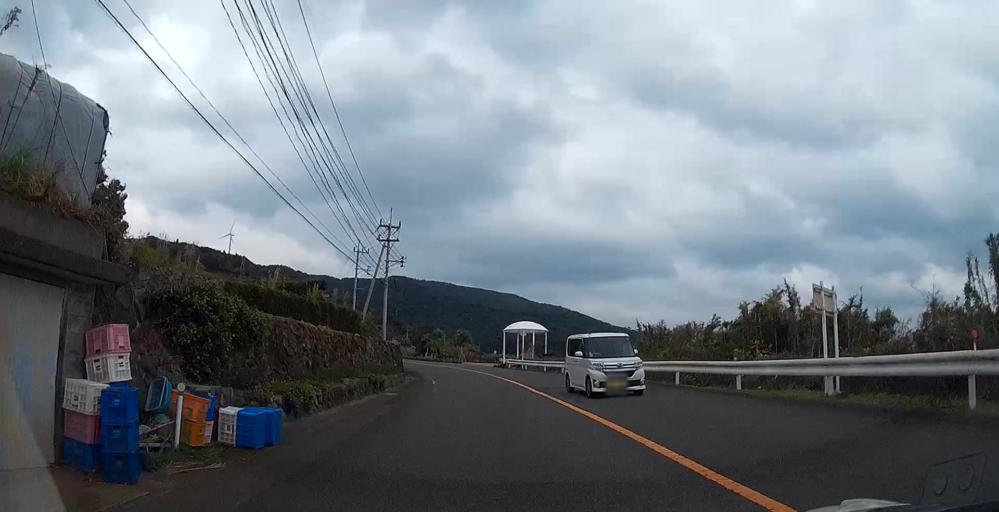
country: JP
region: Kagoshima
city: Akune
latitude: 32.1070
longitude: 130.1458
